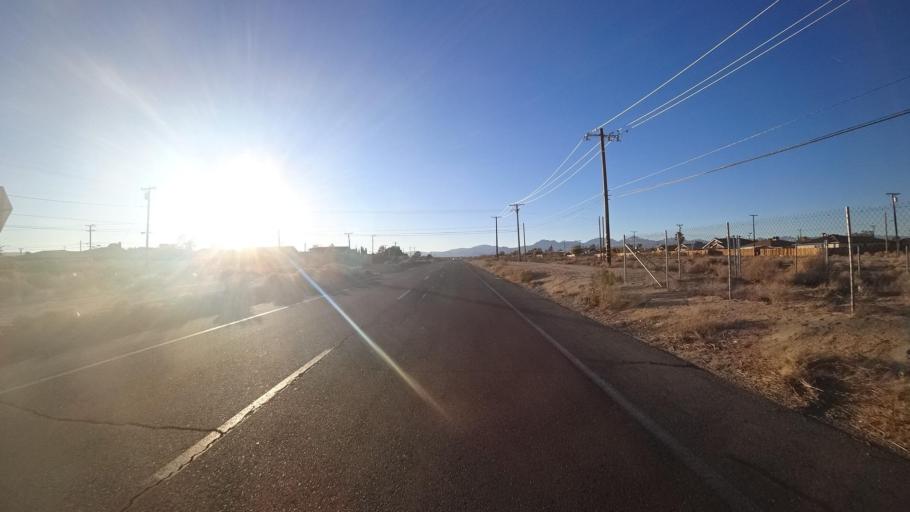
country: US
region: California
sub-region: Kern County
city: Ridgecrest
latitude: 35.6078
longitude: -117.6890
